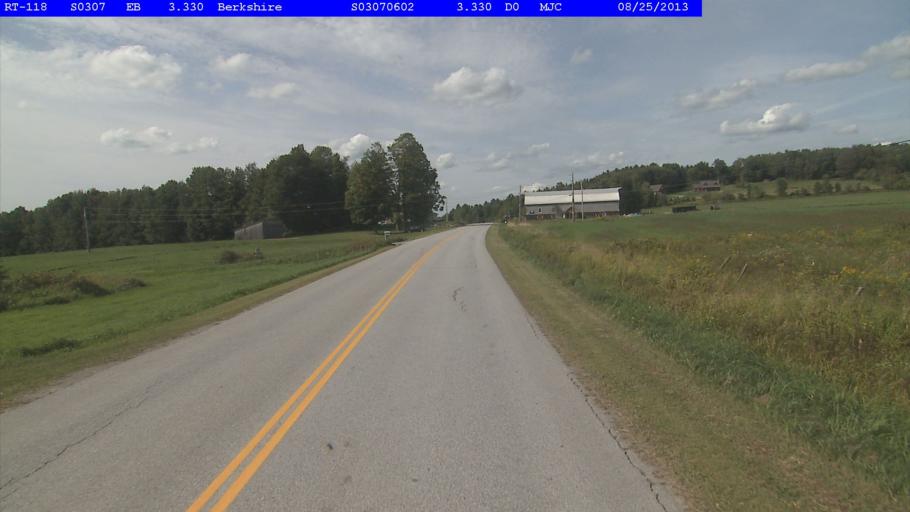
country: US
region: Vermont
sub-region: Franklin County
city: Enosburg Falls
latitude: 44.9634
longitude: -72.7590
